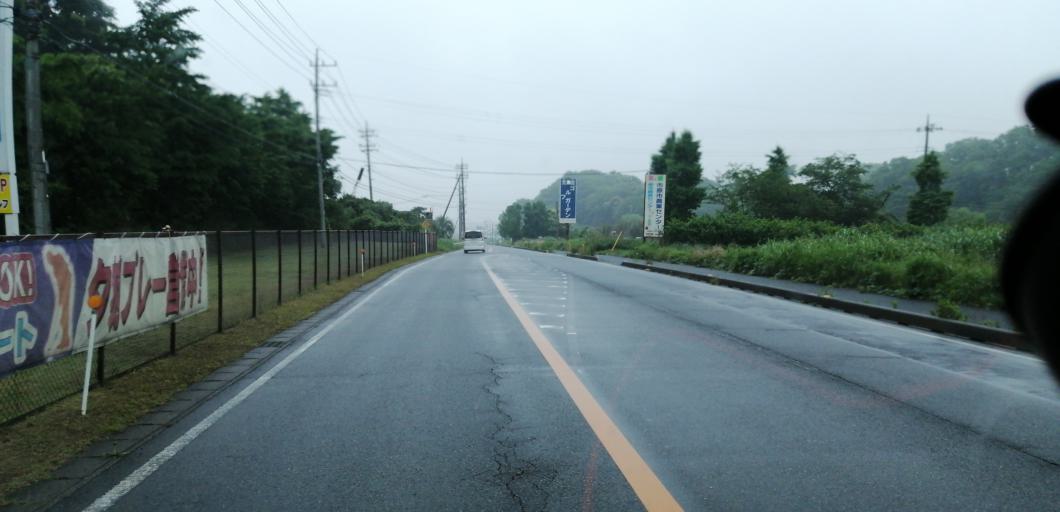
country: JP
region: Chiba
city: Ichihara
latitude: 35.4617
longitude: 140.1079
